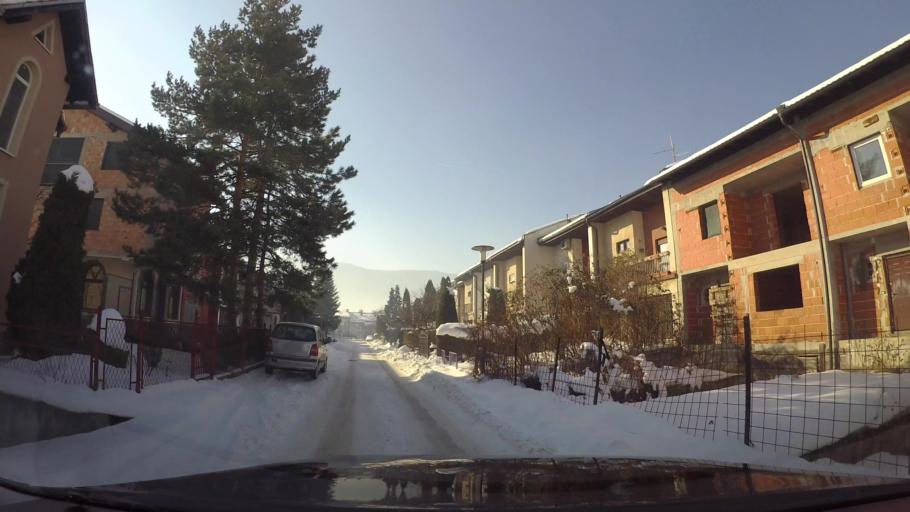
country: BA
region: Federation of Bosnia and Herzegovina
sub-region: Kanton Sarajevo
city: Sarajevo
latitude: 43.8152
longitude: 18.3185
